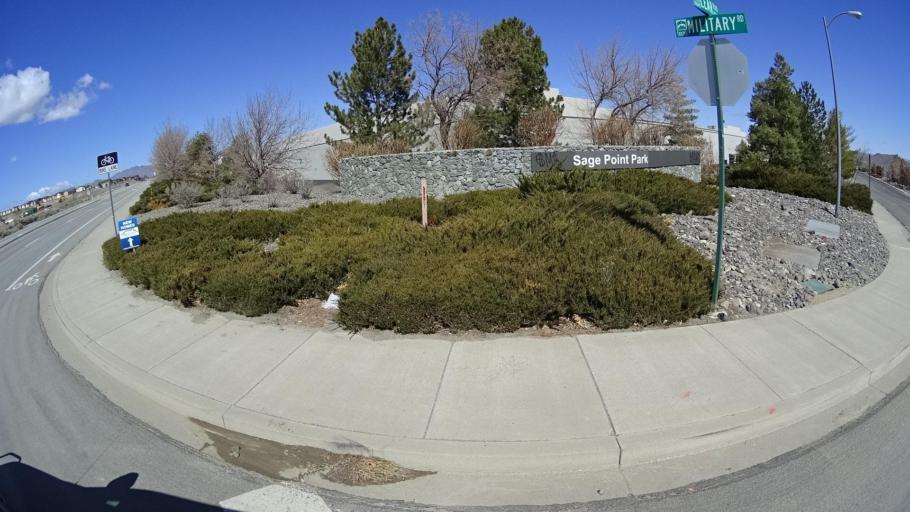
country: US
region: Nevada
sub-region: Washoe County
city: Lemmon Valley
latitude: 39.6441
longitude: -119.8641
